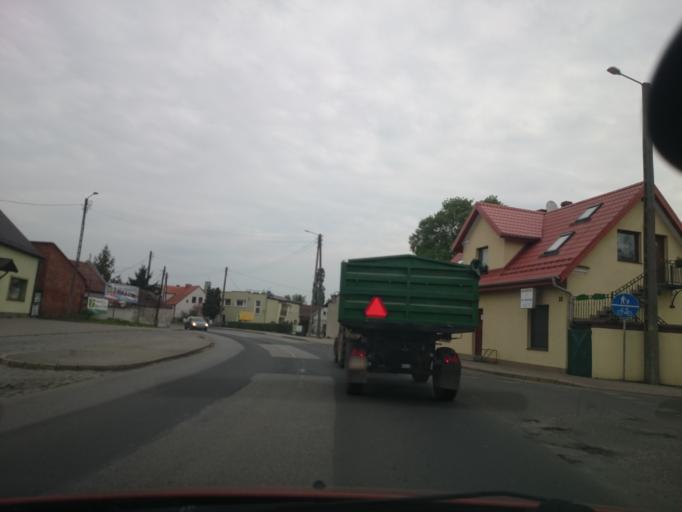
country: PL
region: Opole Voivodeship
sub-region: Powiat opolski
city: Dobrzen Wielki
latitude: 50.7615
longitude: 17.8437
